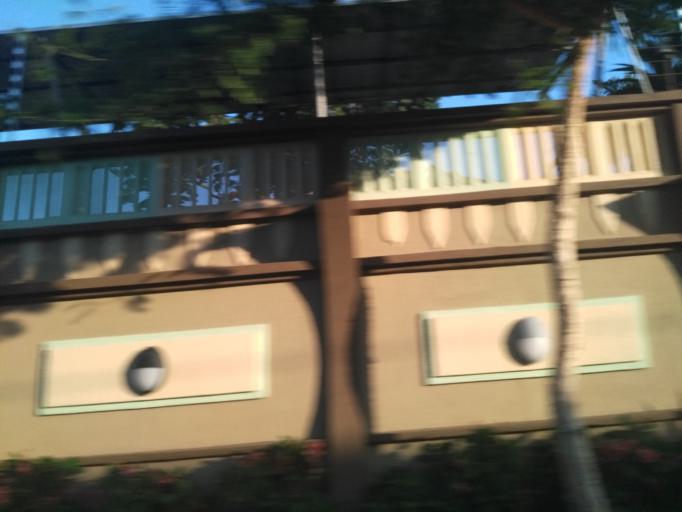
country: TZ
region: Dar es Salaam
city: Magomeni
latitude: -6.7795
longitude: 39.2834
